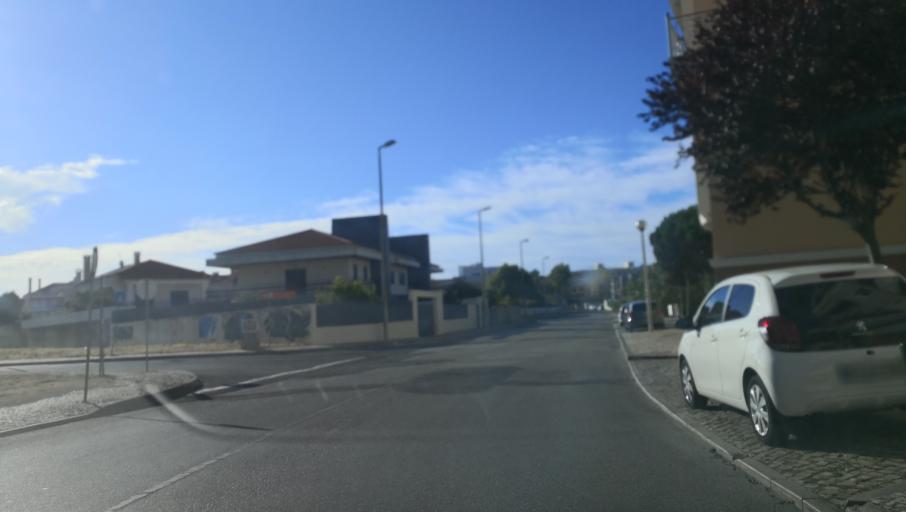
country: PT
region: Lisbon
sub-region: Oeiras
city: Carcavelos
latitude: 38.6846
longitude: -9.3261
